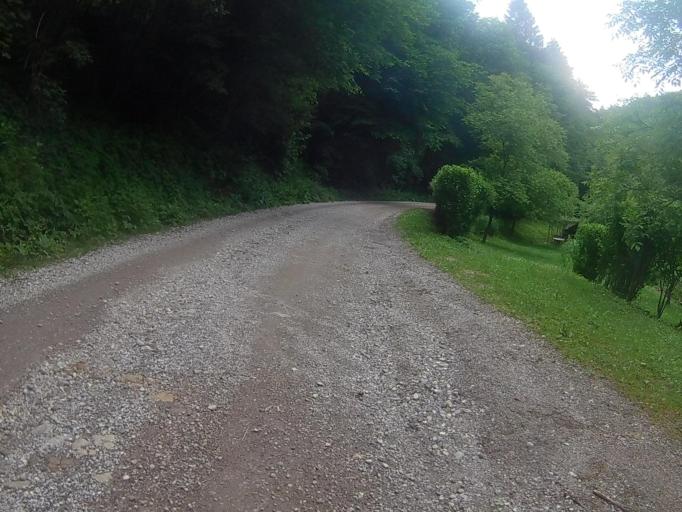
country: SI
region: Maribor
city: Bresternica
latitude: 46.6111
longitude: 15.5692
